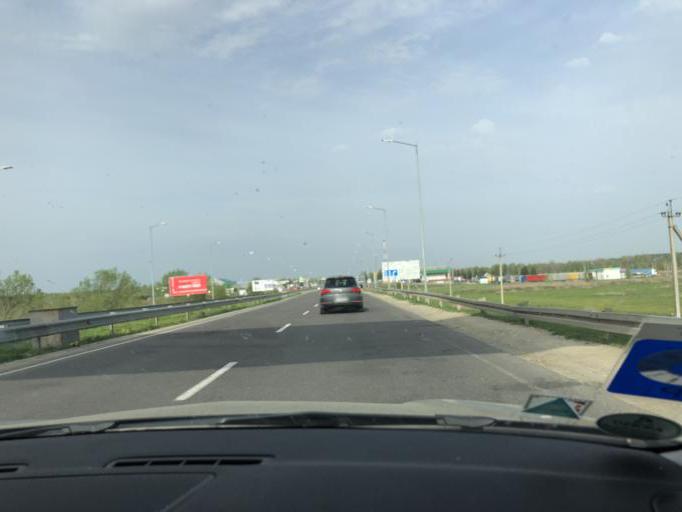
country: PL
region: Subcarpathian Voivodeship
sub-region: Powiat lubaczowski
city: Wielkie Oczy
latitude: 49.9563
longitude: 23.1291
